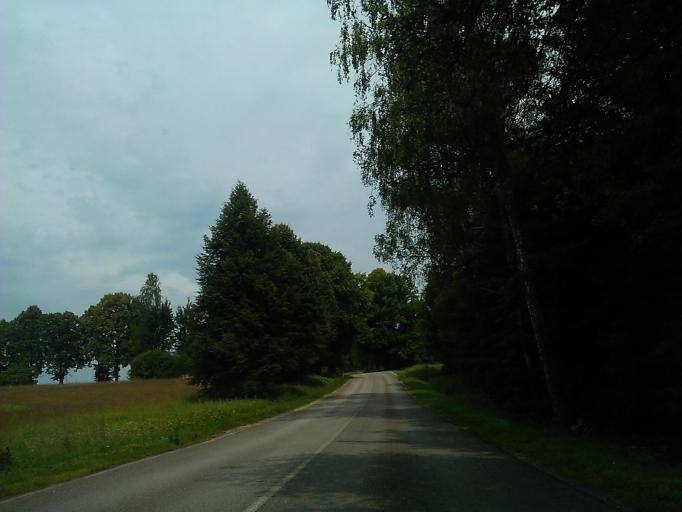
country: LV
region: Beverina
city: Murmuiza
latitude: 57.4260
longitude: 25.4390
